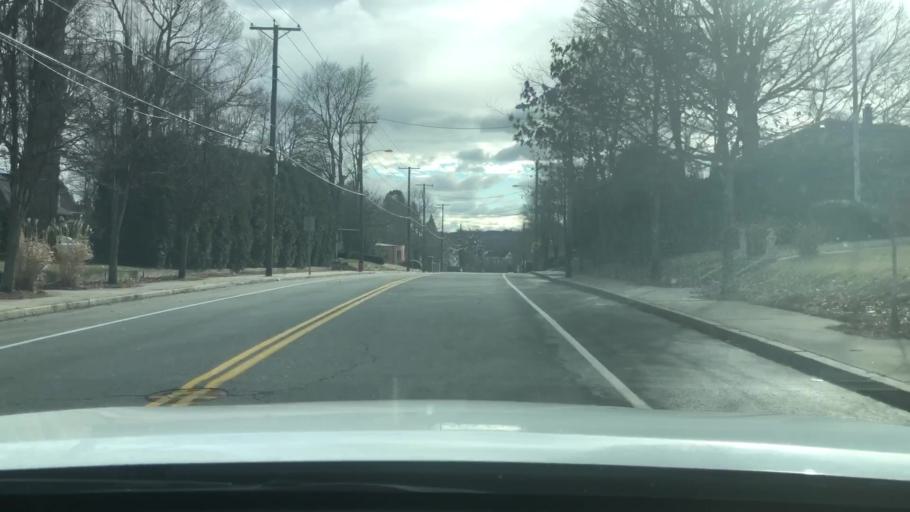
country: US
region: Rhode Island
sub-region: Providence County
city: Woonsocket
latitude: 42.0078
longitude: -71.5217
